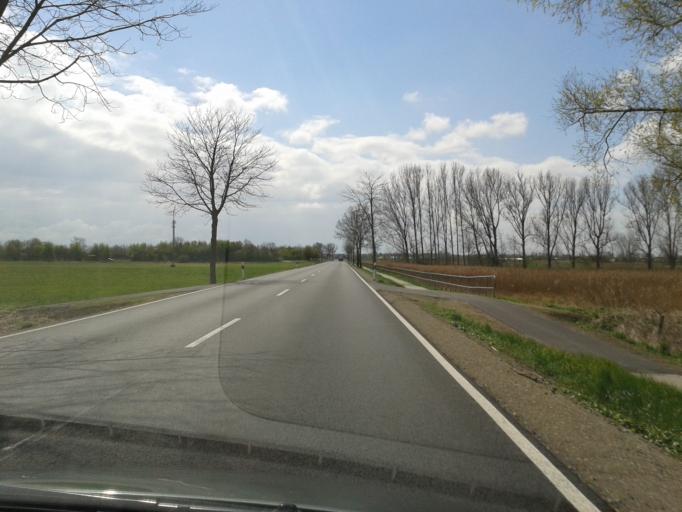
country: DE
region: Saxony-Anhalt
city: Salzwedel
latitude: 52.8796
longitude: 11.1690
